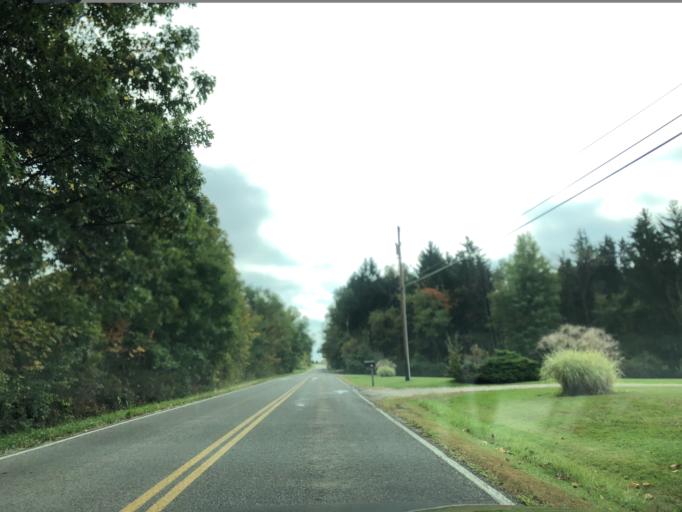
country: US
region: Ohio
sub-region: Summit County
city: Boston Heights
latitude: 41.2671
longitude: -81.5176
